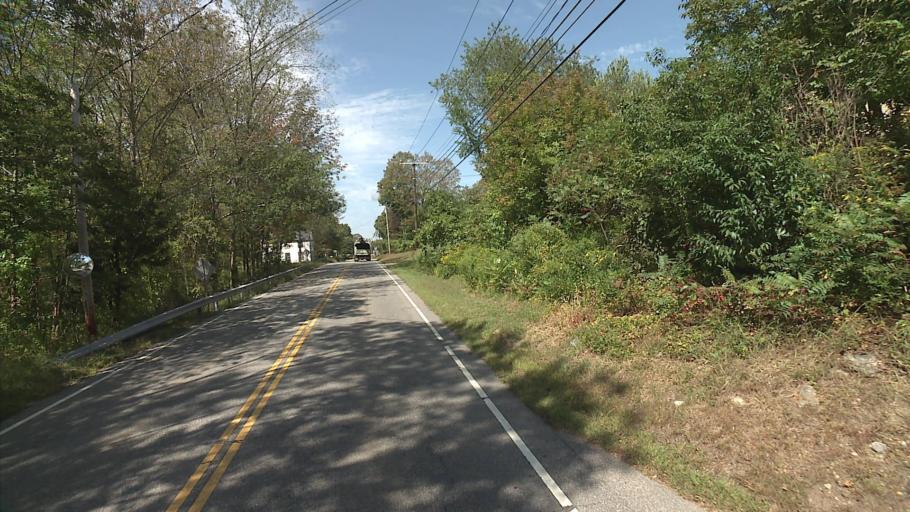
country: US
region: Connecticut
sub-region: Tolland County
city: South Coventry
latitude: 41.6984
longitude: -72.2999
